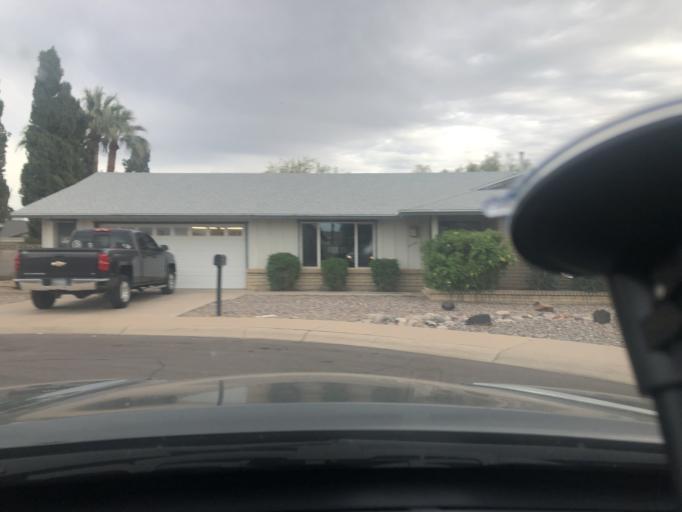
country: US
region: Arizona
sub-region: Maricopa County
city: Scottsdale
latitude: 33.4872
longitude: -111.8995
